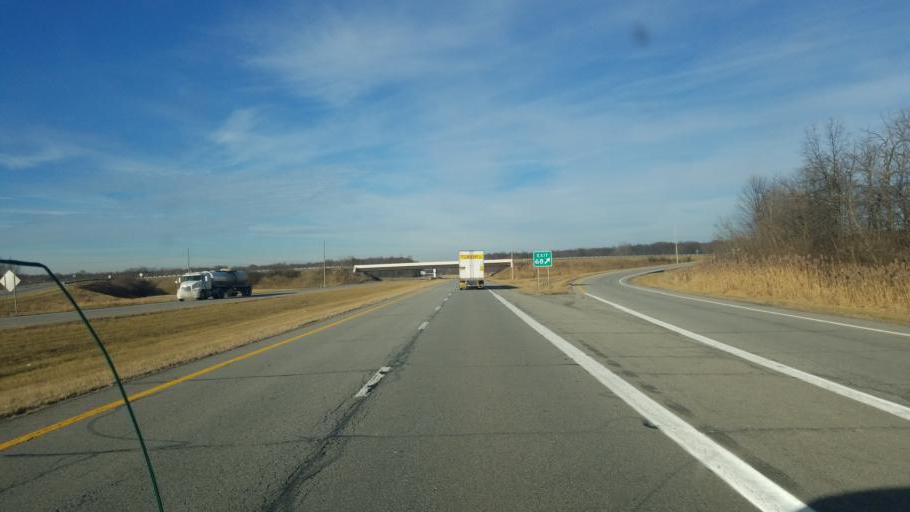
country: US
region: Ohio
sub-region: Trumbull County
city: Cortland
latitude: 41.4596
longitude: -80.7128
